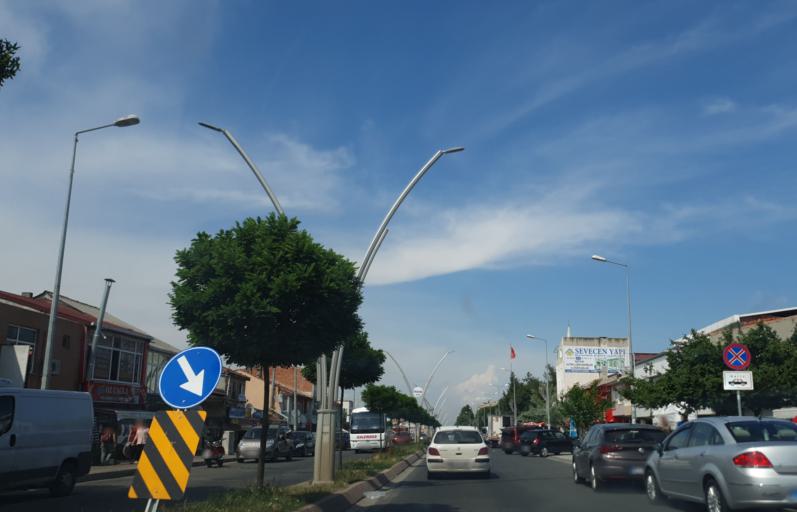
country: TR
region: Tekirdag
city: Marmaracik
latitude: 41.2351
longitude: 27.7072
